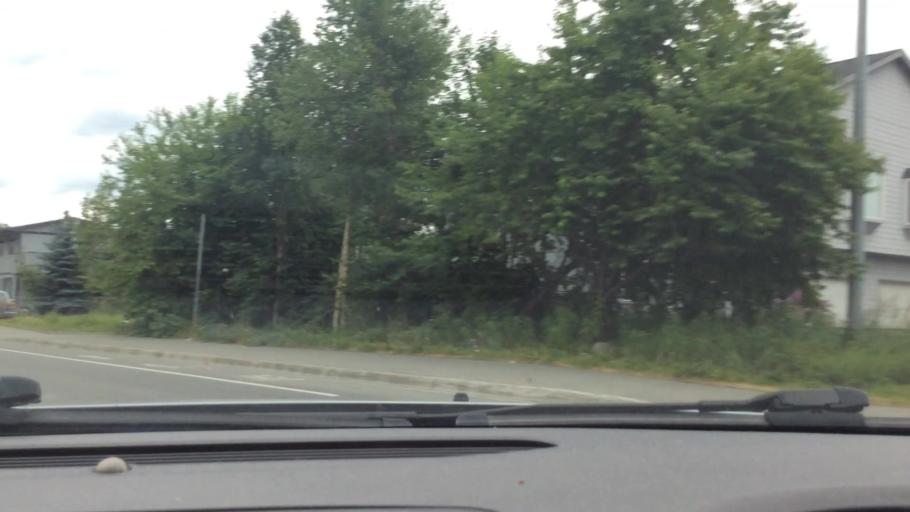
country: US
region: Alaska
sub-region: Anchorage Municipality
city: Elmendorf Air Force Base
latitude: 61.2138
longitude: -149.7559
